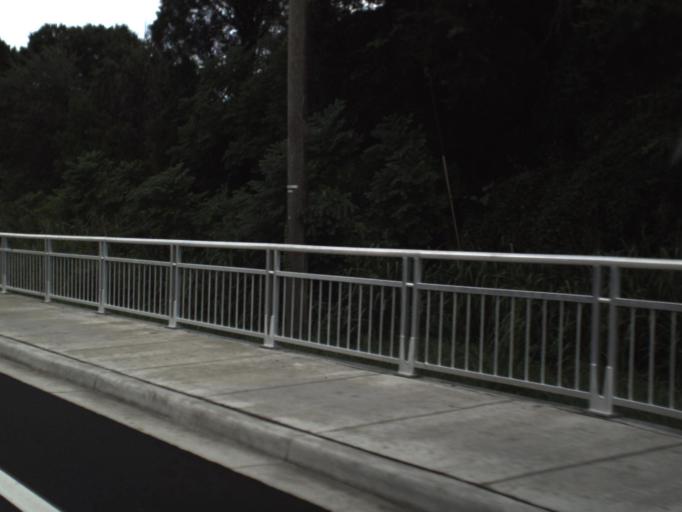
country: US
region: Florida
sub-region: Polk County
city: Mulberry
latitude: 27.8869
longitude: -81.9734
